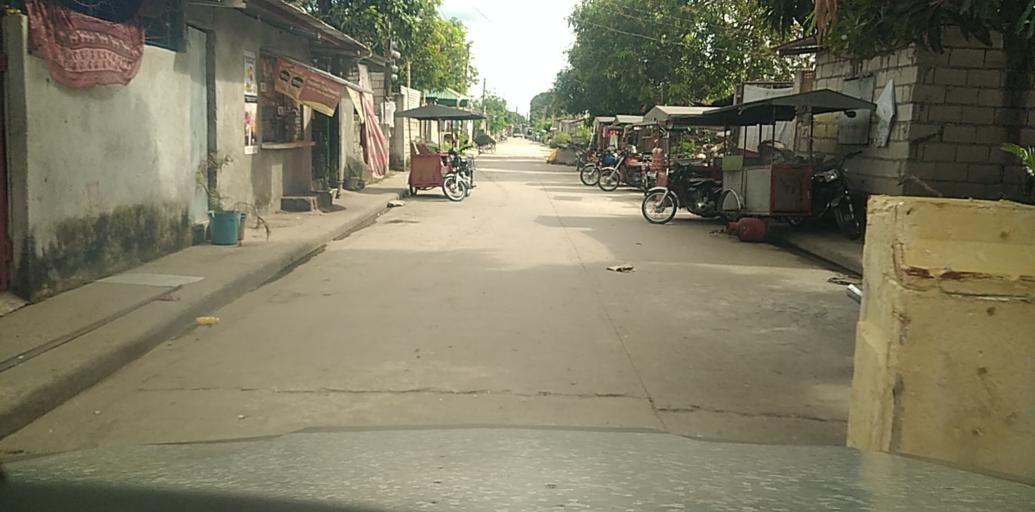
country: PH
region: Central Luzon
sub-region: Province of Pampanga
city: Buensuseso
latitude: 15.1812
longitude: 120.6680
